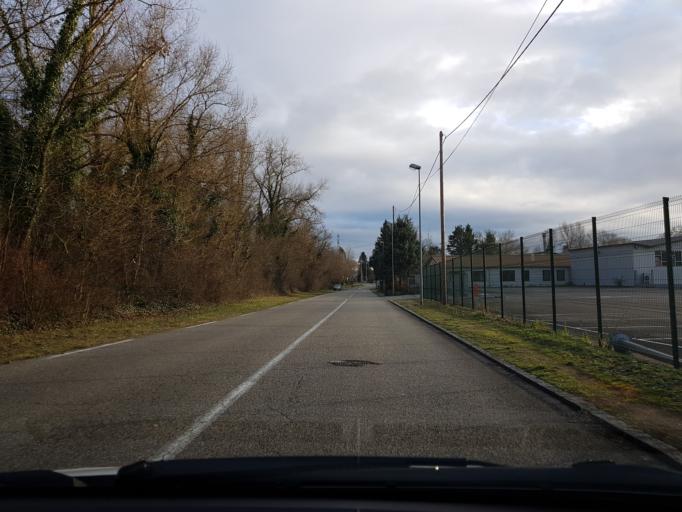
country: FR
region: Alsace
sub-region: Departement du Haut-Rhin
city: Kembs
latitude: 47.6613
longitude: 7.5130
